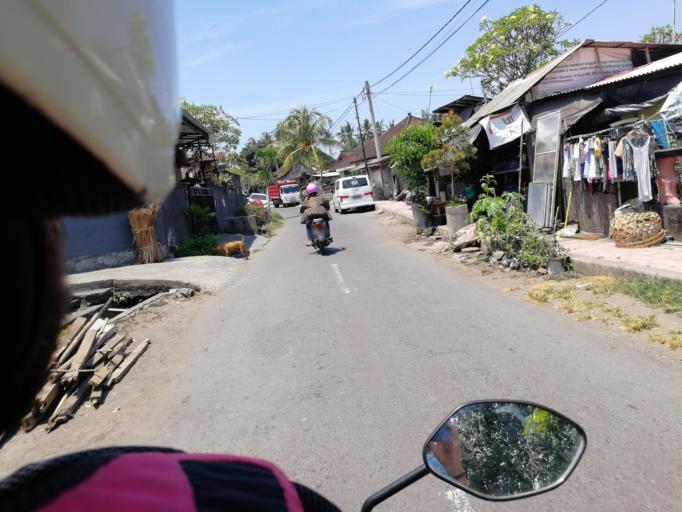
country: ID
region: Bali
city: Subagan
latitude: -8.4613
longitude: 115.5979
